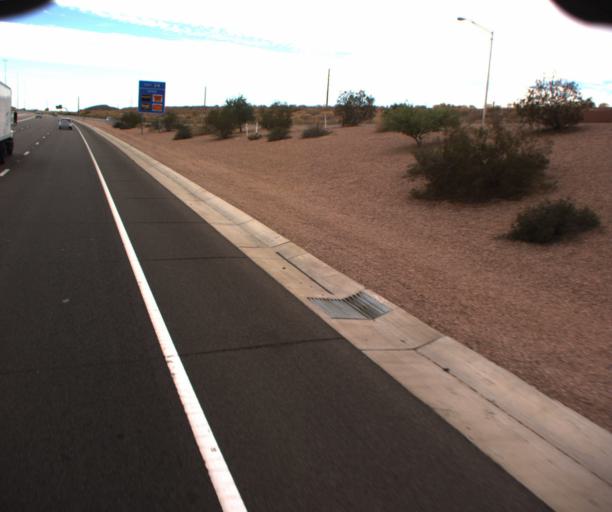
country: US
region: Arizona
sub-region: Pinal County
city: Apache Junction
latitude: 33.4647
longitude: -111.6791
